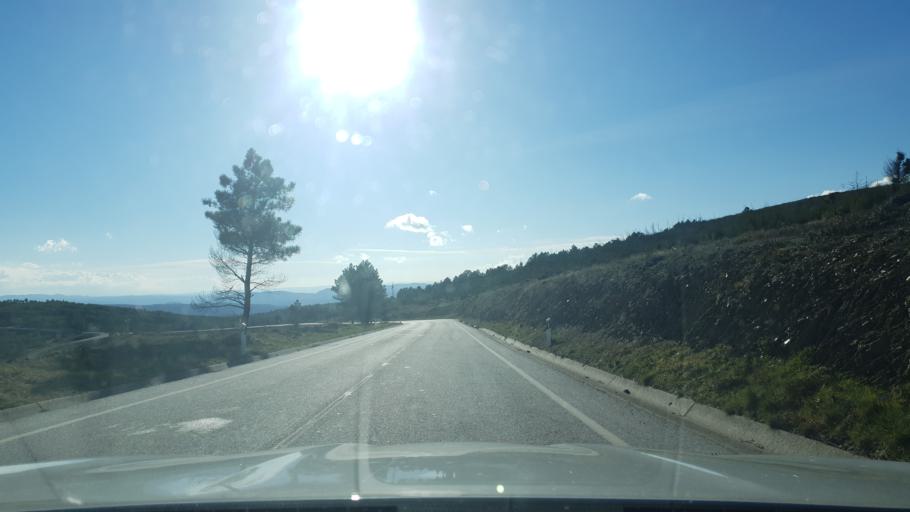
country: PT
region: Braganca
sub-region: Freixo de Espada A Cinta
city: Freixo de Espada a Cinta
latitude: 41.1503
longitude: -6.8049
